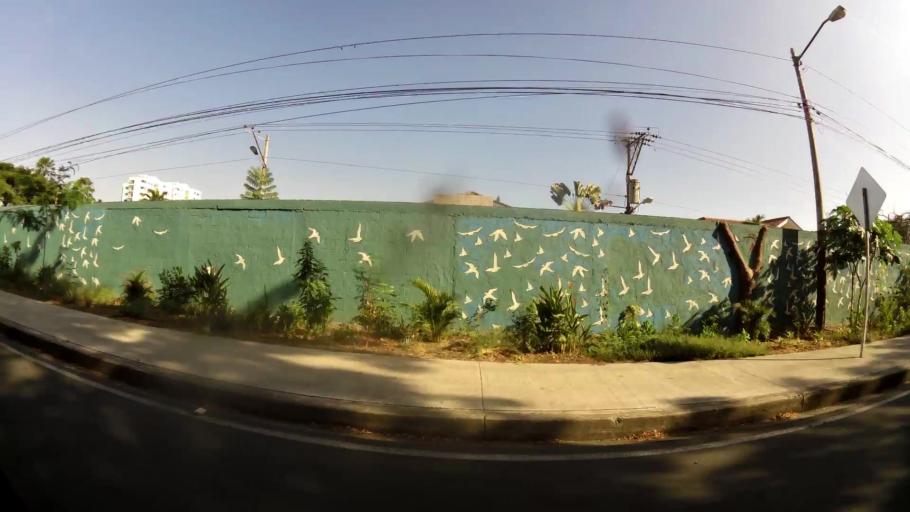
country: EC
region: Guayas
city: Santa Lucia
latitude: -2.1862
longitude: -79.9678
